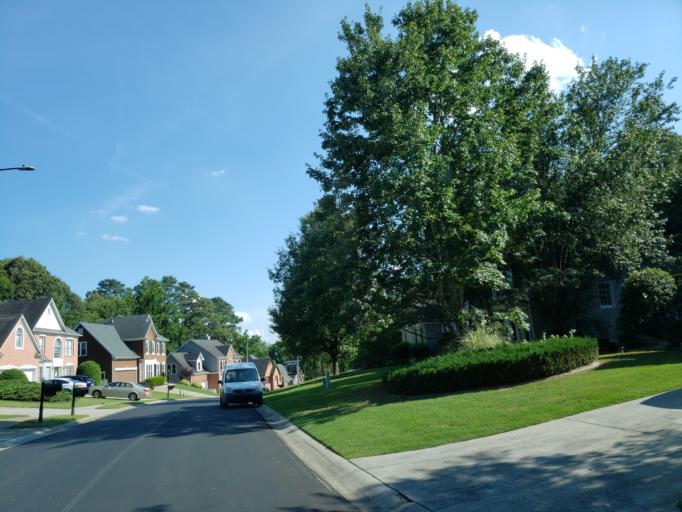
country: US
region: Georgia
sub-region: Cherokee County
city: Woodstock
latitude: 34.1221
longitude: -84.5300
